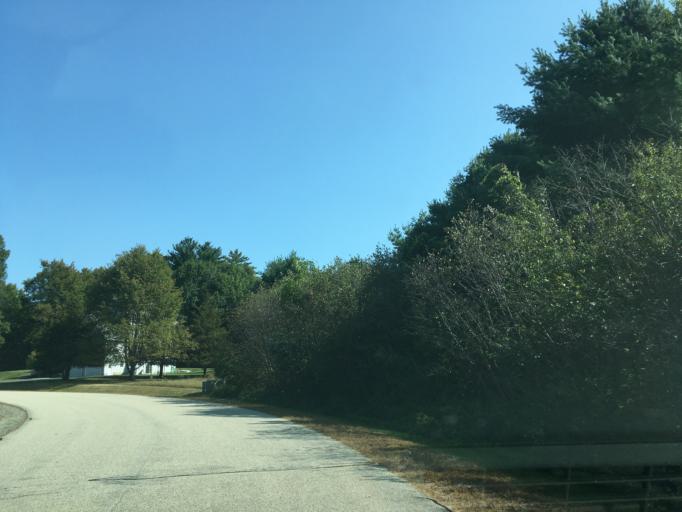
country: US
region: New Hampshire
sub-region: Rockingham County
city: Stratham Station
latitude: 43.0096
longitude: -70.8881
